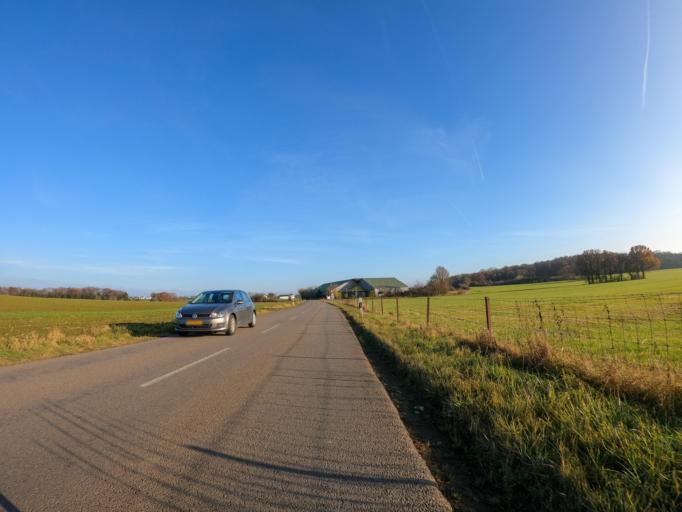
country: LU
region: Luxembourg
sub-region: Canton de Capellen
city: Garnich
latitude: 49.5999
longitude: 5.9343
